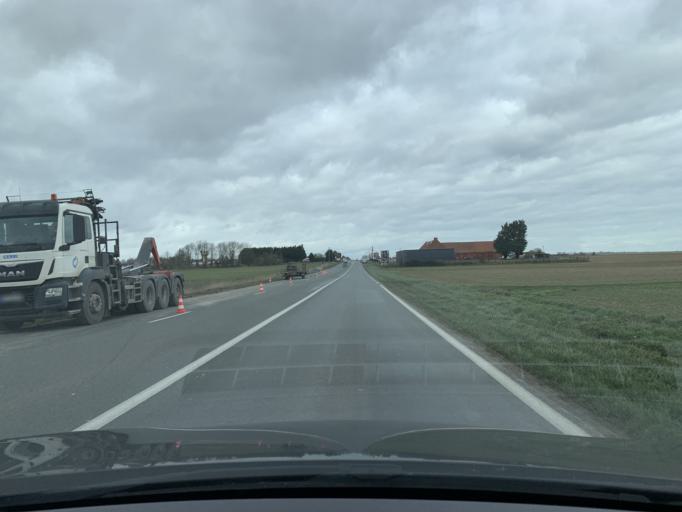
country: FR
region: Nord-Pas-de-Calais
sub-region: Departement du Nord
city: Raillencourt-Sainte-Olle
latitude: 50.2227
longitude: 3.1775
